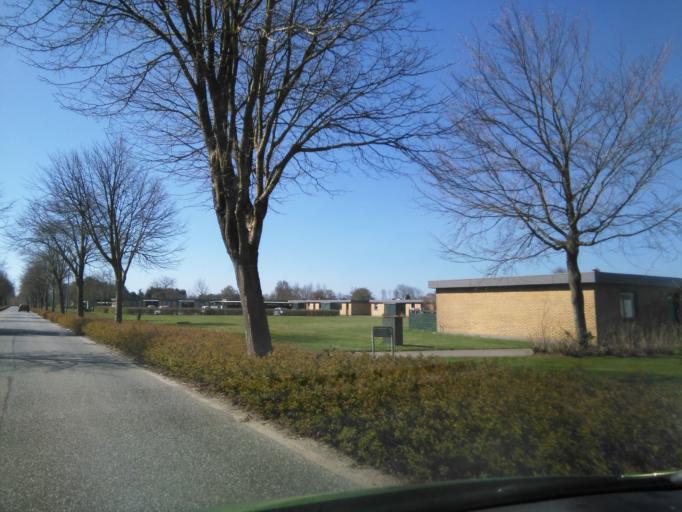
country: DK
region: South Denmark
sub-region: Billund Kommune
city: Billund
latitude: 55.7264
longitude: 9.1156
